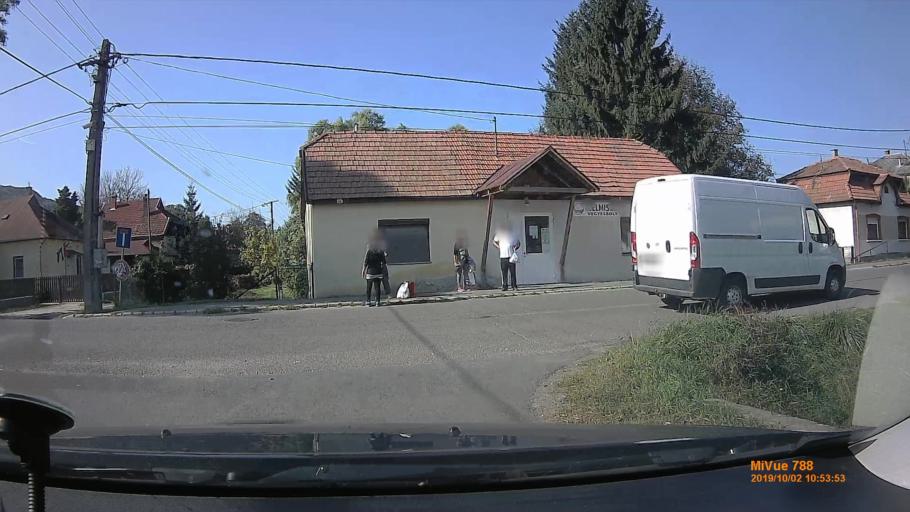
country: HU
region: Nograd
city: Matraverebely
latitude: 47.9725
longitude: 19.7792
